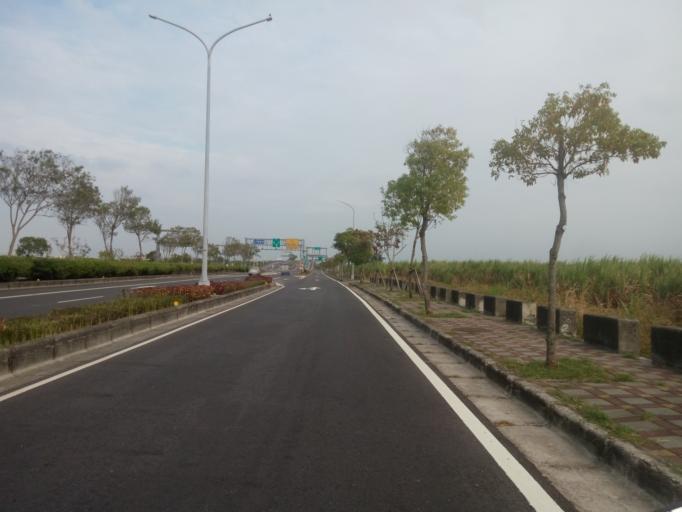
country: TW
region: Taiwan
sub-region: Chiayi
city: Taibao
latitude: 23.4832
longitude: 120.3724
